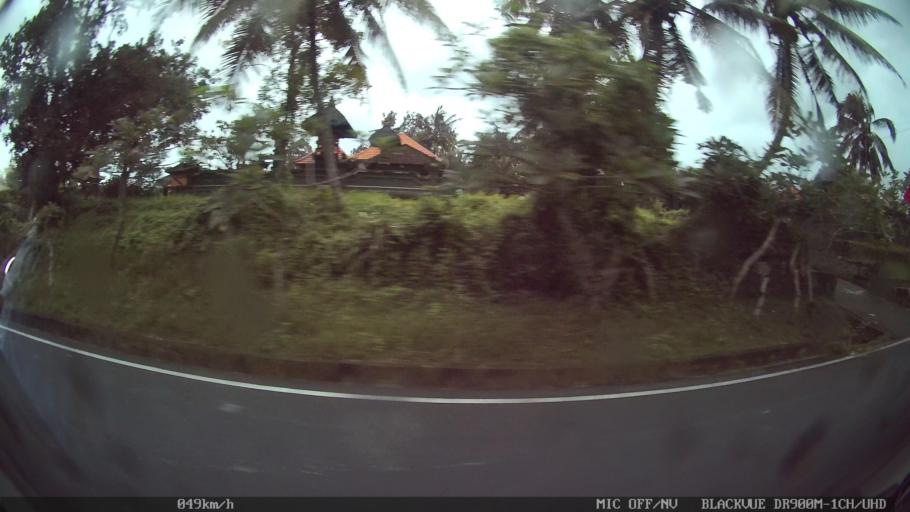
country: ID
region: Bali
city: Banjar Sayanbaleran
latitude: -8.5228
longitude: 115.1864
